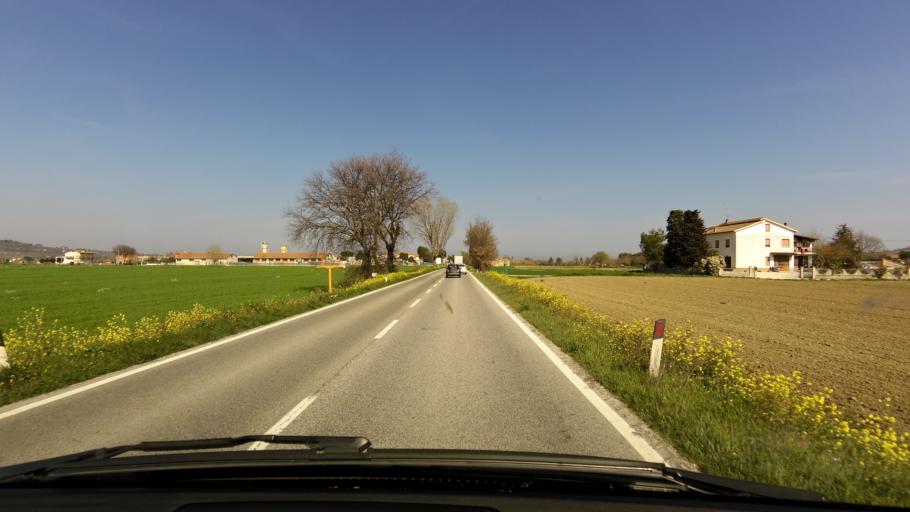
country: IT
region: The Marches
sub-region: Provincia di Macerata
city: Potenza Picena
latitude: 43.3891
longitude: 13.6301
